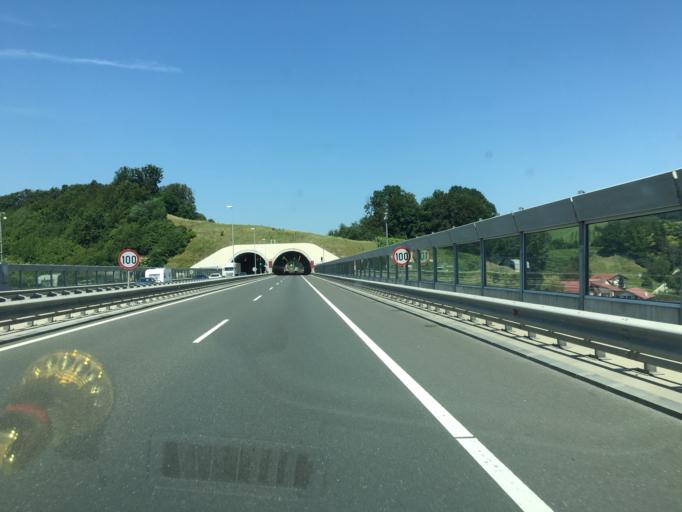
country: SI
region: Maribor
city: Maribor
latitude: 46.5556
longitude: 15.6893
